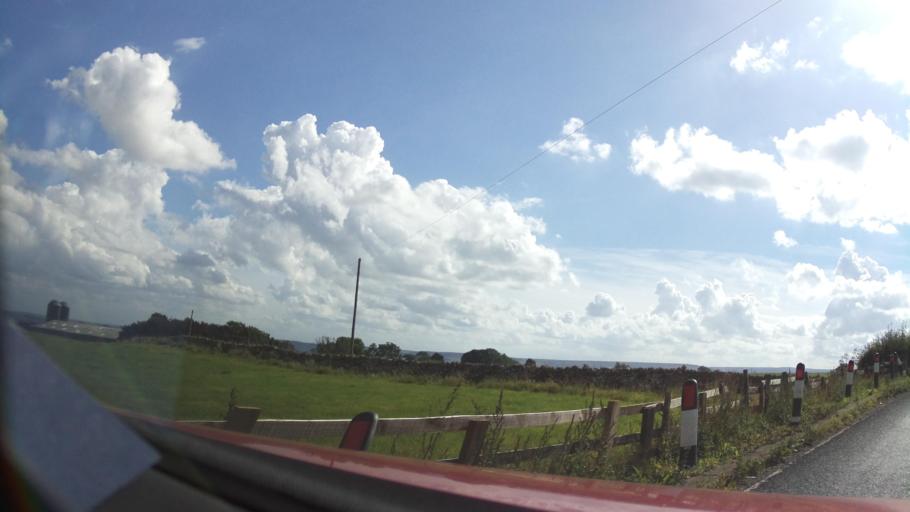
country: GB
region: England
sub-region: North Yorkshire
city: Leyburn
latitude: 54.3450
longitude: -1.8136
